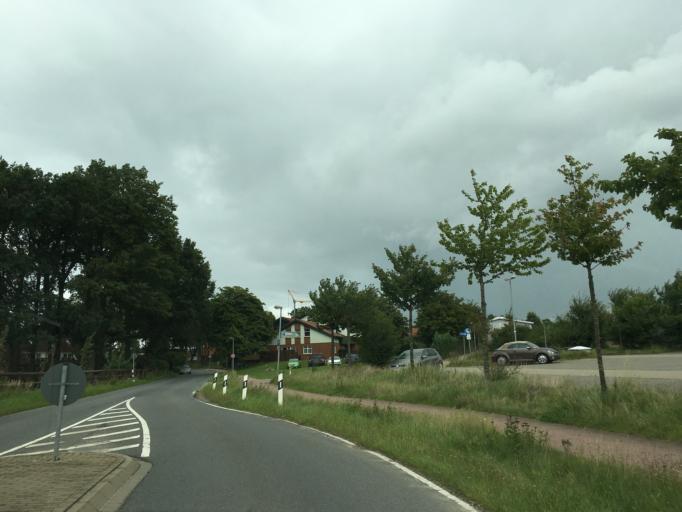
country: DE
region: Lower Saxony
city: Melbeck
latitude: 53.2099
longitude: 10.3854
